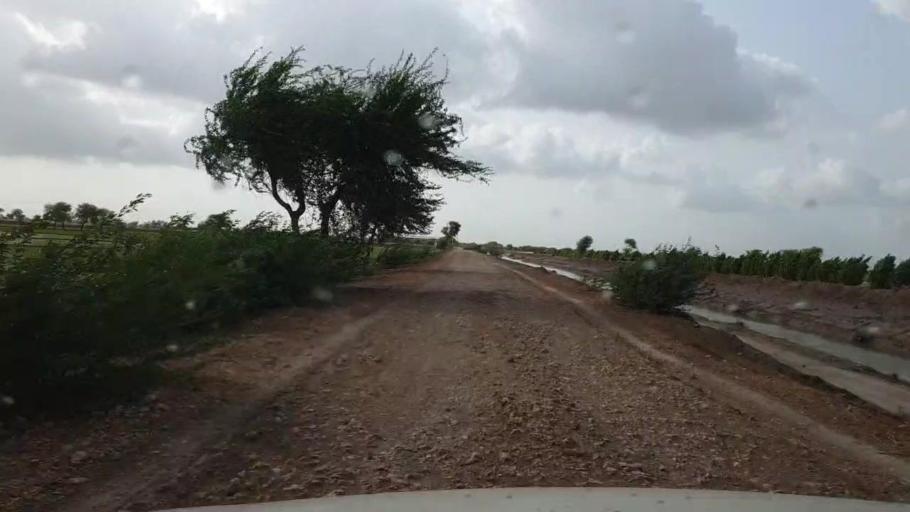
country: PK
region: Sindh
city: Kario
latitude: 24.7789
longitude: 68.5898
